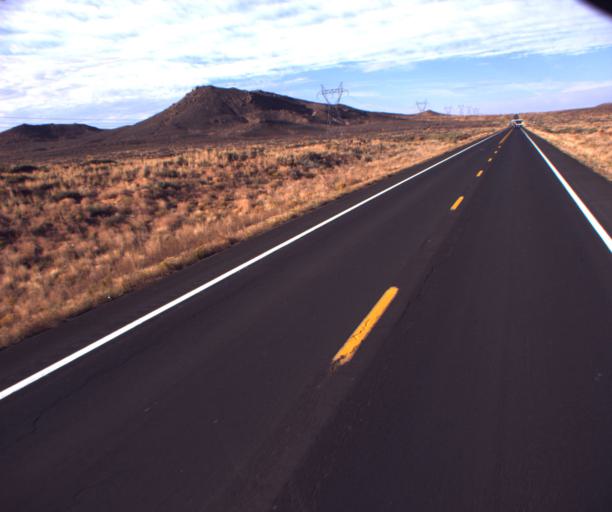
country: US
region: Arizona
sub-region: Apache County
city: Lukachukai
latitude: 36.9614
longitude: -109.4874
